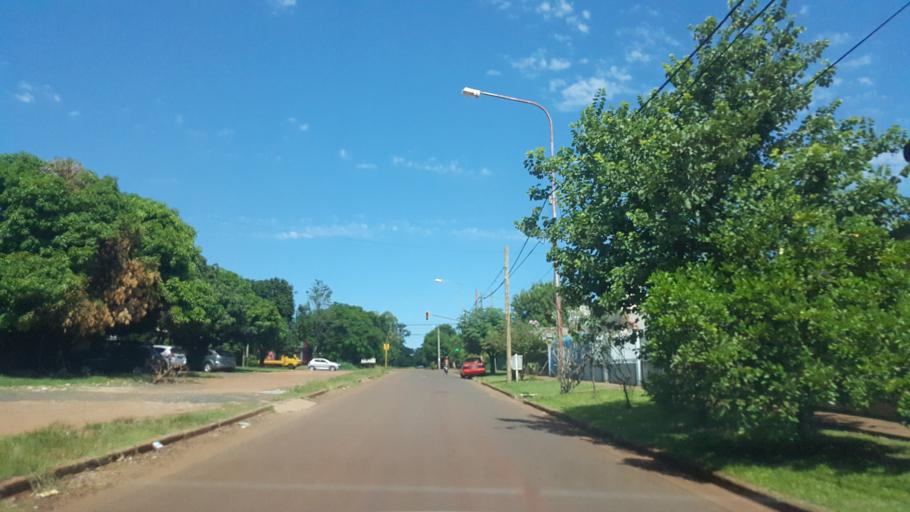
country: AR
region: Misiones
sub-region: Departamento de Capital
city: Posadas
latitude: -27.3842
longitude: -55.9228
